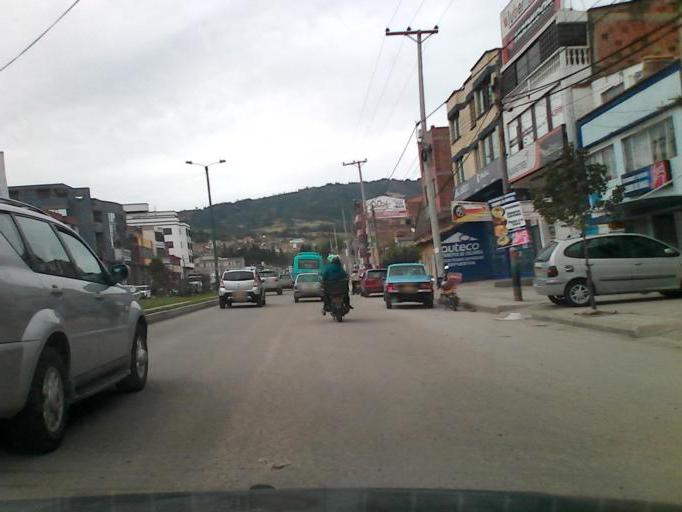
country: CO
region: Boyaca
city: Duitama
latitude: 5.8201
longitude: -73.0358
